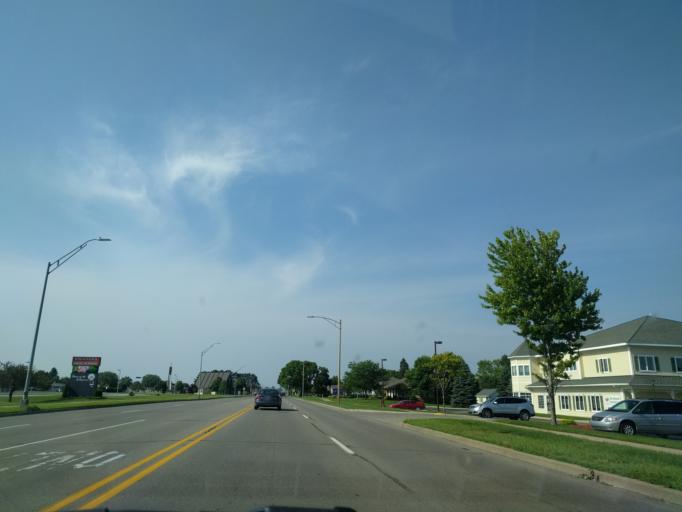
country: US
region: Michigan
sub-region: Delta County
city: Escanaba
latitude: 45.7399
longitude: -87.0798
